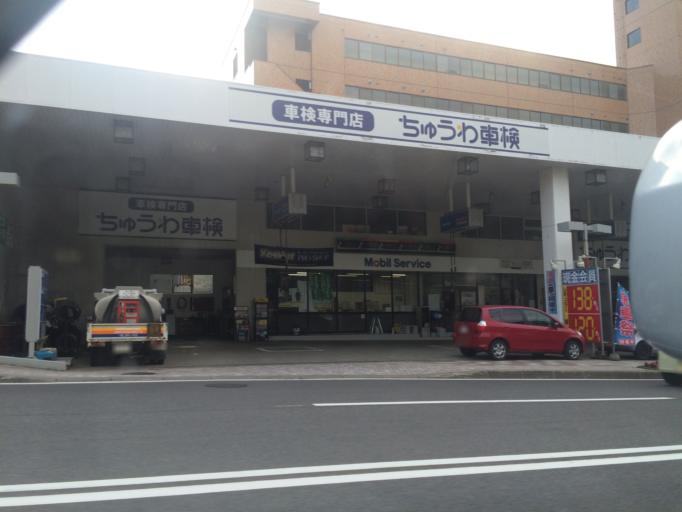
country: JP
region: Hokkaido
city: Sapporo
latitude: 43.0035
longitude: 141.3483
